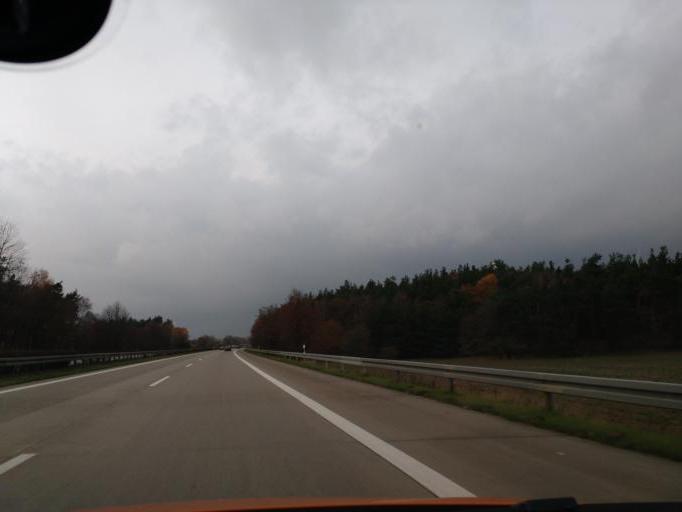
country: DE
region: Brandenburg
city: Wittstock
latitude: 53.1406
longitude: 12.4254
